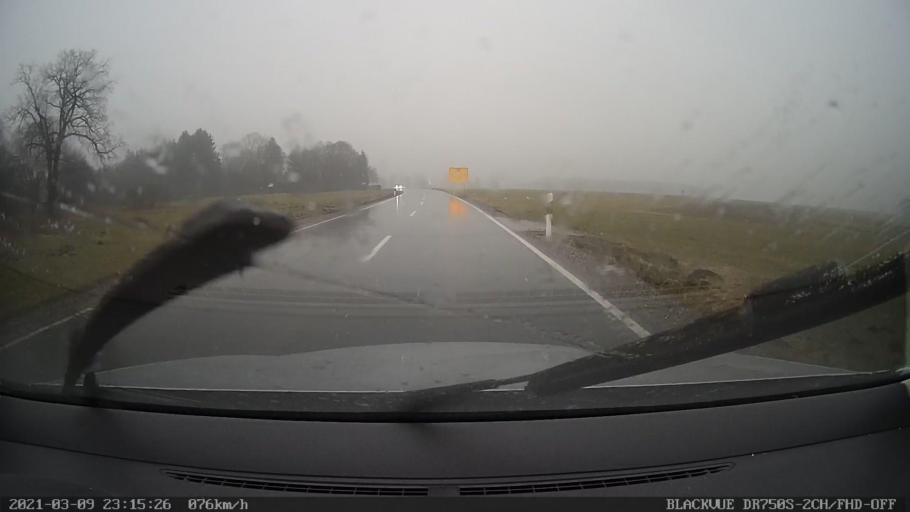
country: DE
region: Bavaria
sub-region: Upper Bavaria
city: Schonstett
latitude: 47.9751
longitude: 12.2279
